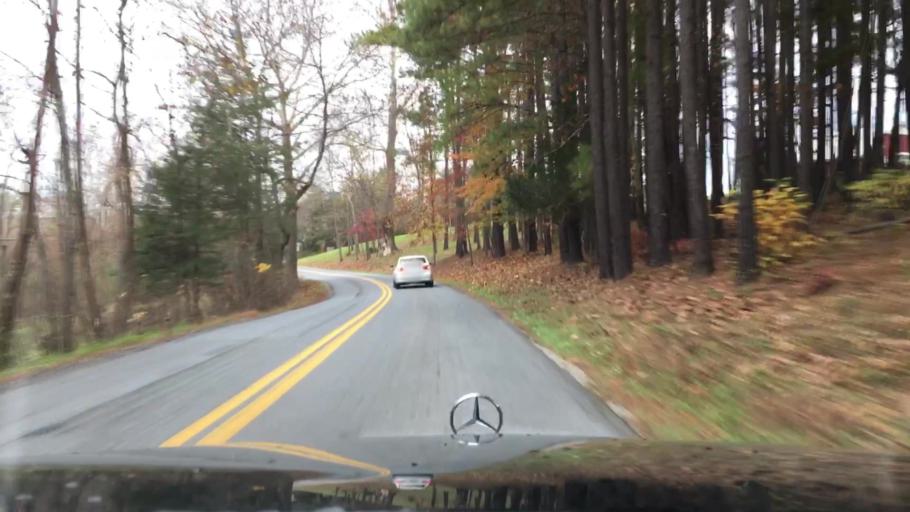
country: US
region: Virginia
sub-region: Campbell County
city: Timberlake
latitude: 37.2815
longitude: -79.2710
